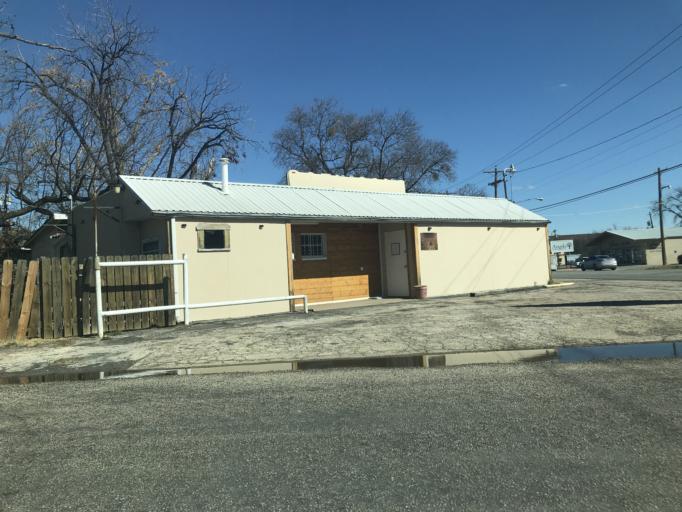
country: US
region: Texas
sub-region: Tom Green County
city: San Angelo
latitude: 31.4433
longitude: -100.4586
